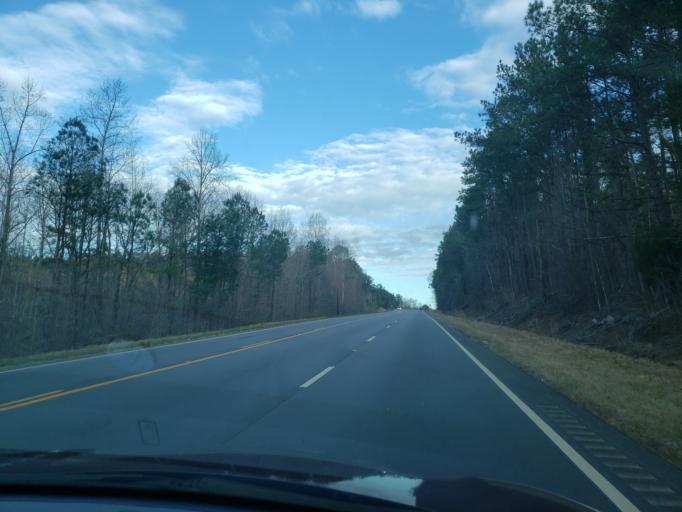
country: US
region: Alabama
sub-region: Randolph County
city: Wedowee
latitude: 33.2485
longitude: -85.4498
